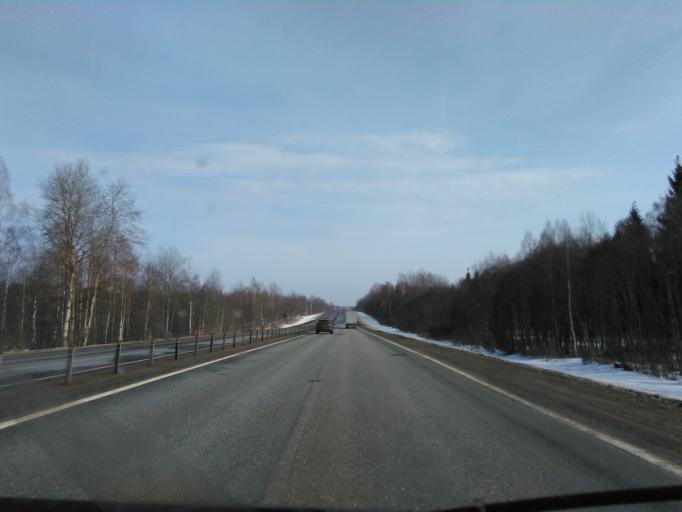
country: BY
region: Vitebsk
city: Dubrowna
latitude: 54.6864
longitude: 30.8378
